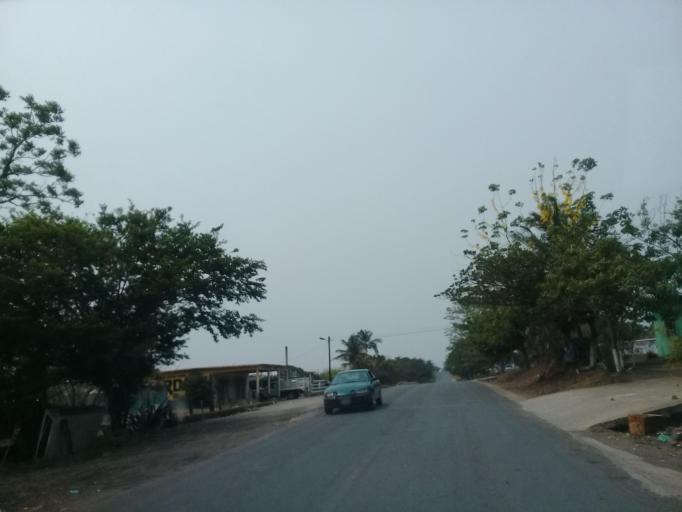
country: MX
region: Veracruz
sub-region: Medellin
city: La Laguna y Monte del Castillo
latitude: 18.9761
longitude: -96.1192
